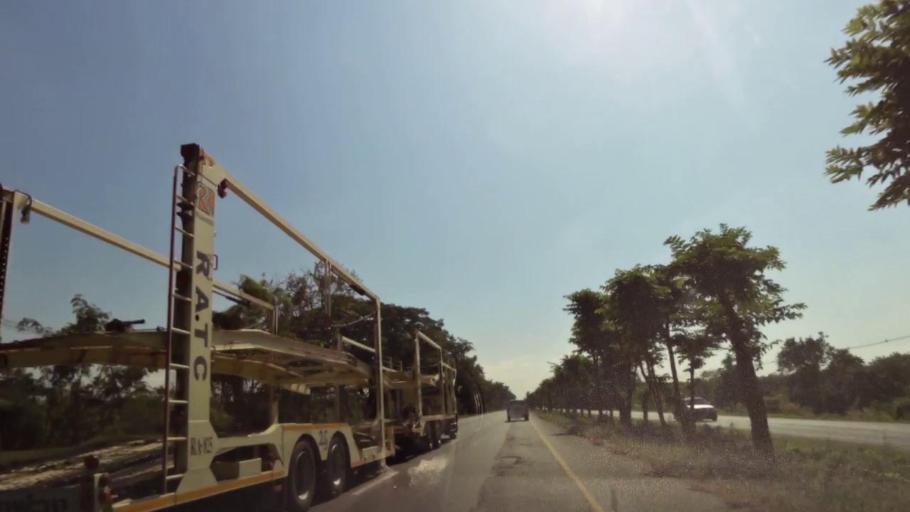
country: TH
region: Nakhon Sawan
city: Kao Liao
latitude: 15.7925
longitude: 100.1206
